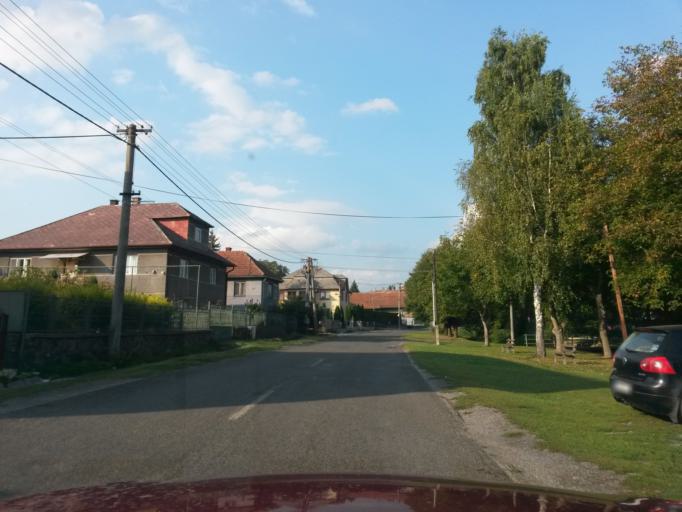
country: SK
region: Kosicky
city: Kosice
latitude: 48.7667
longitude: 21.4450
